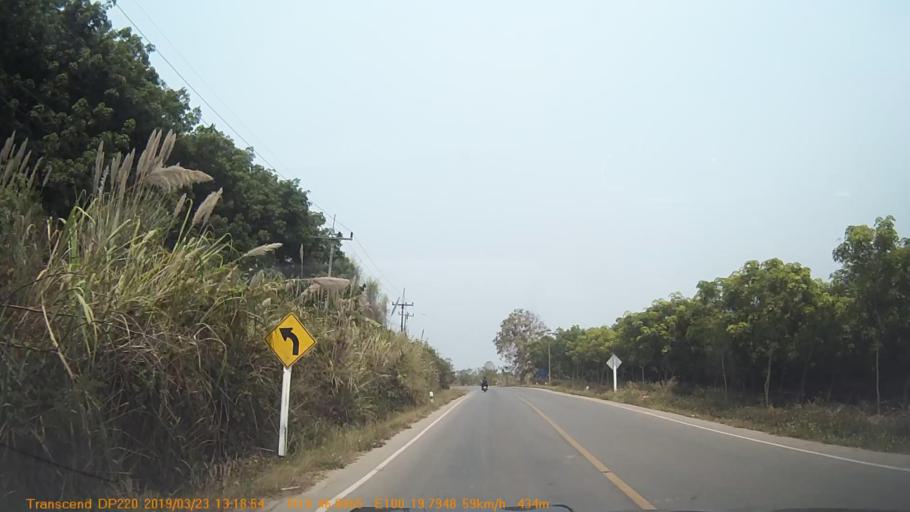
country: TH
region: Chiang Rai
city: Khun Tan
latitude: 19.7818
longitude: 100.3301
